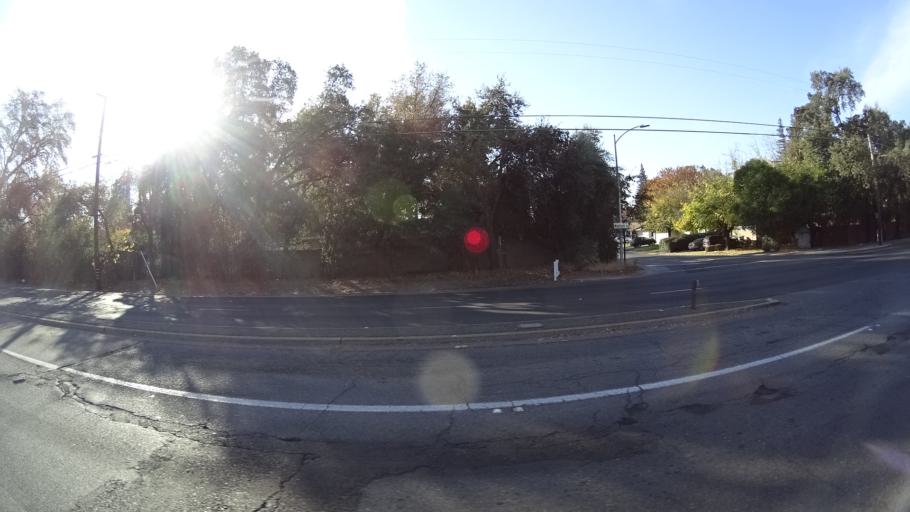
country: US
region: California
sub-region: Sacramento County
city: Fair Oaks
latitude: 38.6640
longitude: -121.2686
